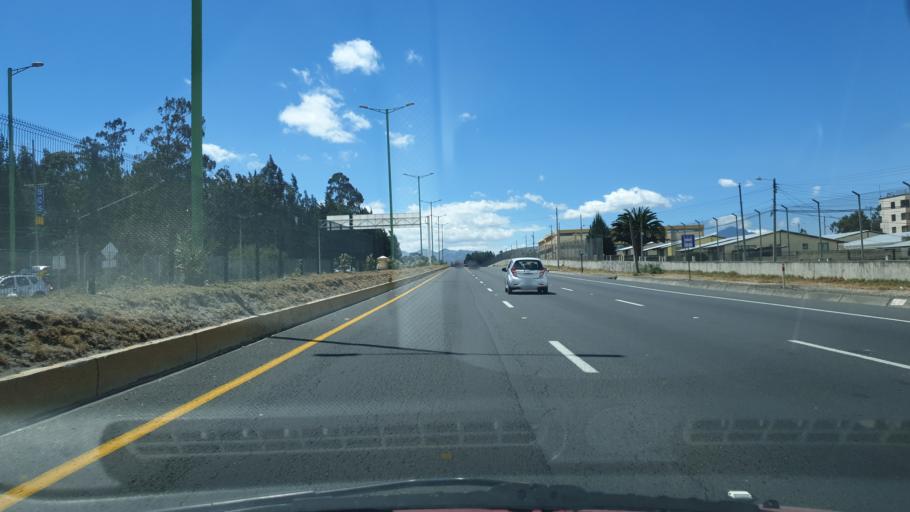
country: EC
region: Cotopaxi
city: Saquisili
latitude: -0.8504
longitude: -78.6195
